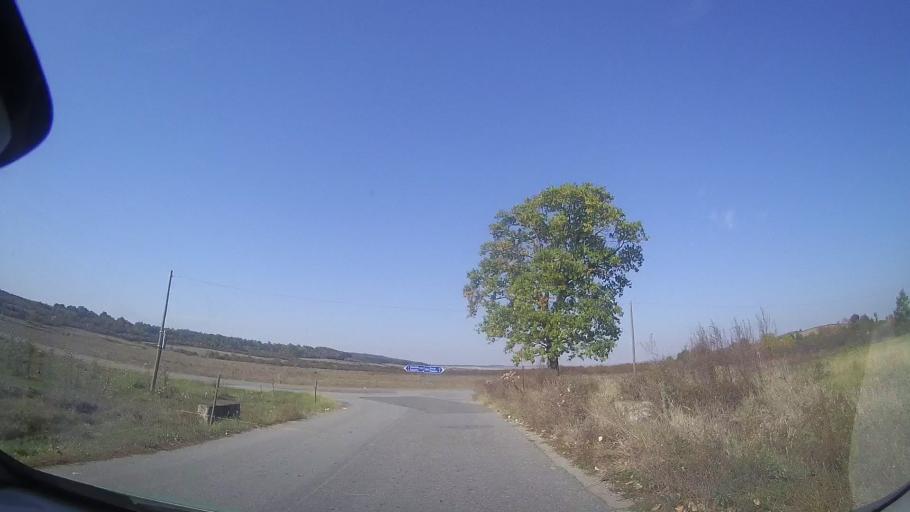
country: RO
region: Timis
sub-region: Comuna Ghizela
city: Ghizela
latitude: 45.8239
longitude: 21.7275
